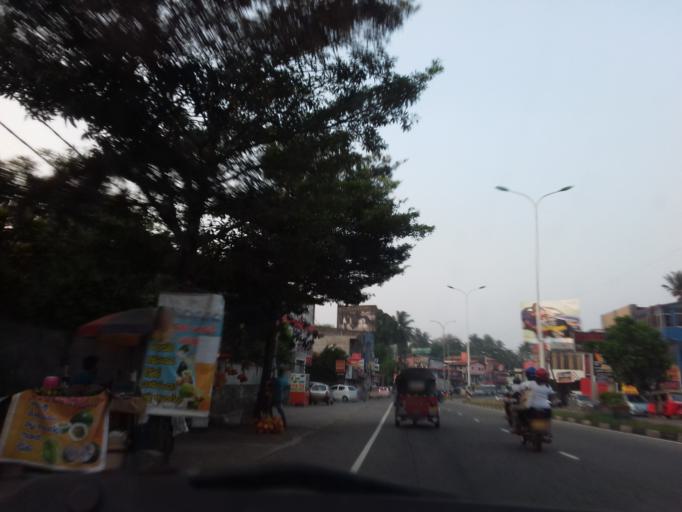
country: LK
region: Western
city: Kelaniya
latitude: 6.9982
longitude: 79.9481
